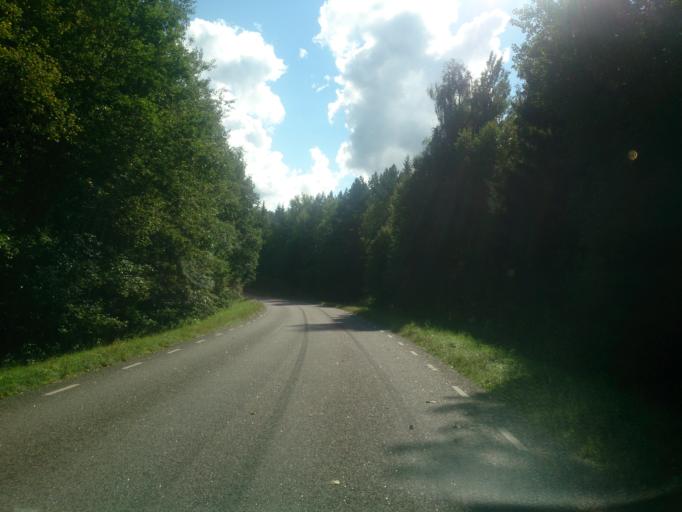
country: SE
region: OEstergoetland
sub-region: Atvidabergs Kommun
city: Atvidaberg
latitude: 58.2400
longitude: 16.0053
